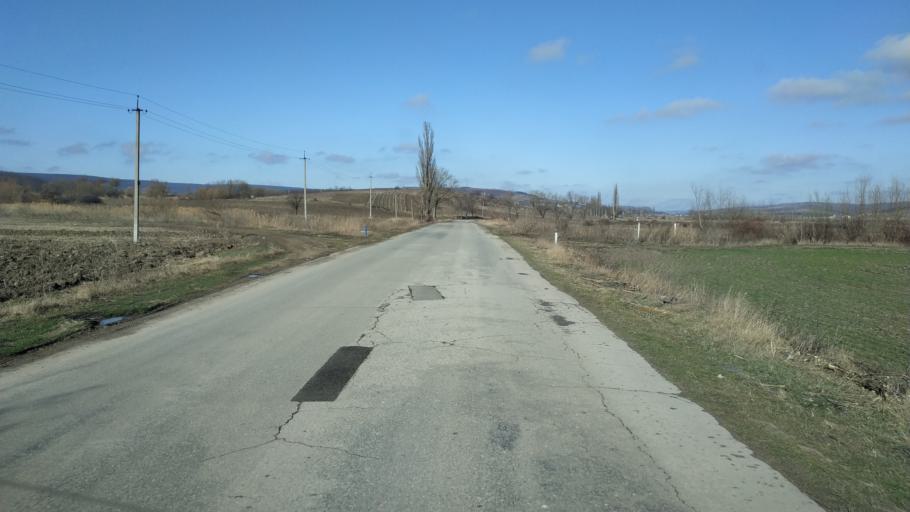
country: MD
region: Hincesti
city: Hincesti
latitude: 46.9405
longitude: 28.6288
